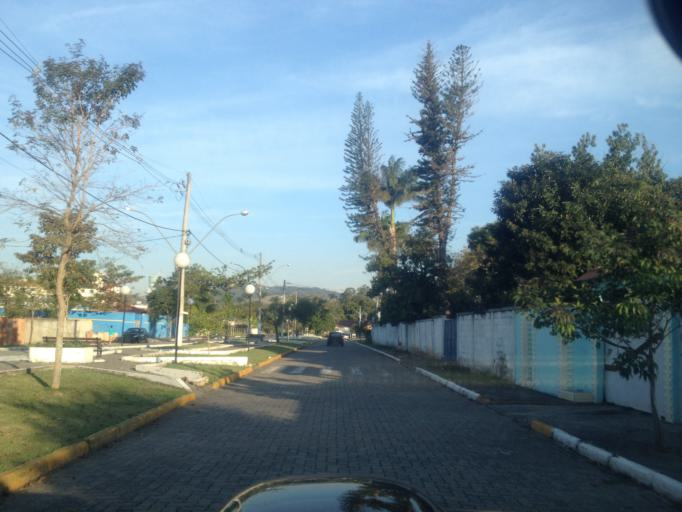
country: BR
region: Rio de Janeiro
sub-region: Porto Real
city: Porto Real
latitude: -22.4193
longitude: -44.2919
